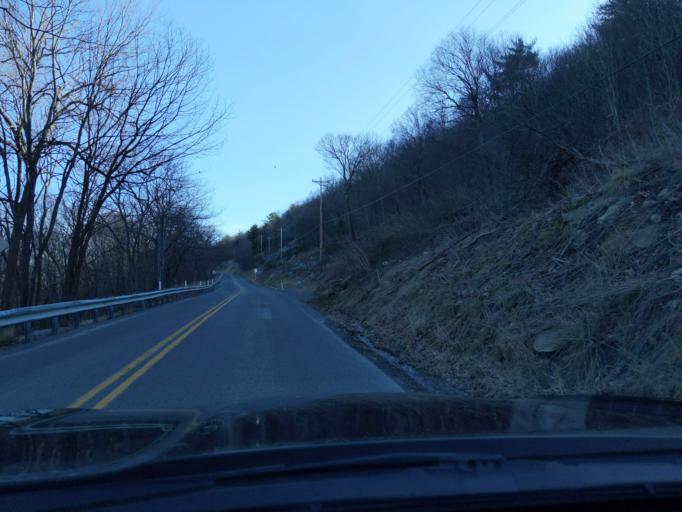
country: US
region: Pennsylvania
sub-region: Blair County
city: Hollidaysburg
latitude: 40.4078
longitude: -78.3014
